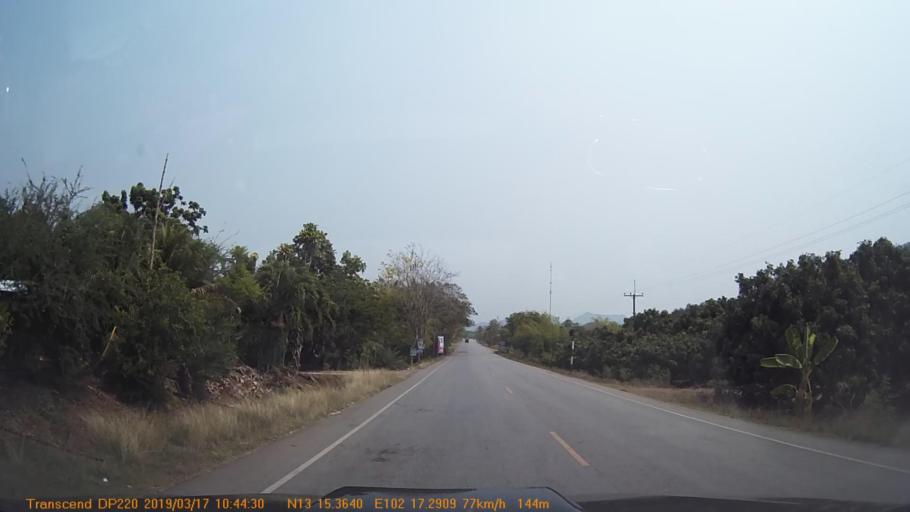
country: TH
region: Sa Kaeo
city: Wang Sombun
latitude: 13.2563
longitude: 102.2883
